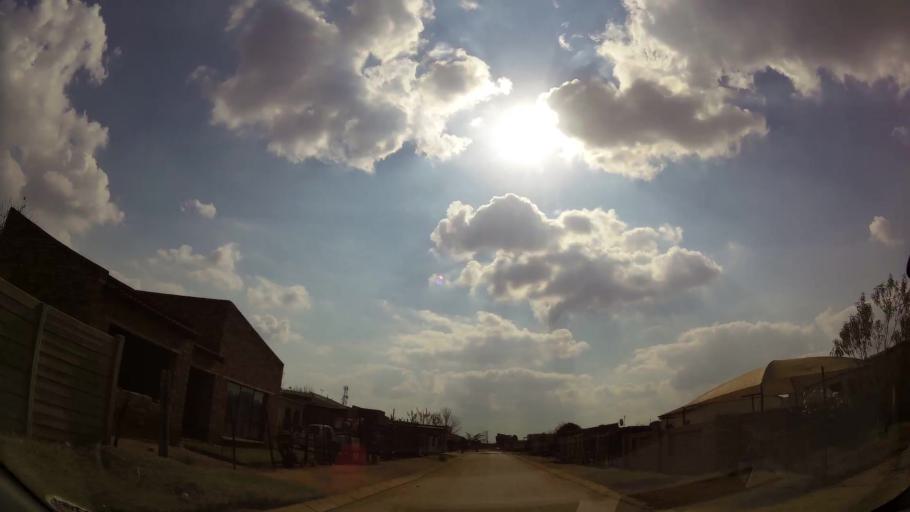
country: ZA
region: Gauteng
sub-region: Ekurhuleni Metropolitan Municipality
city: Springs
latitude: -26.1300
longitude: 28.4743
